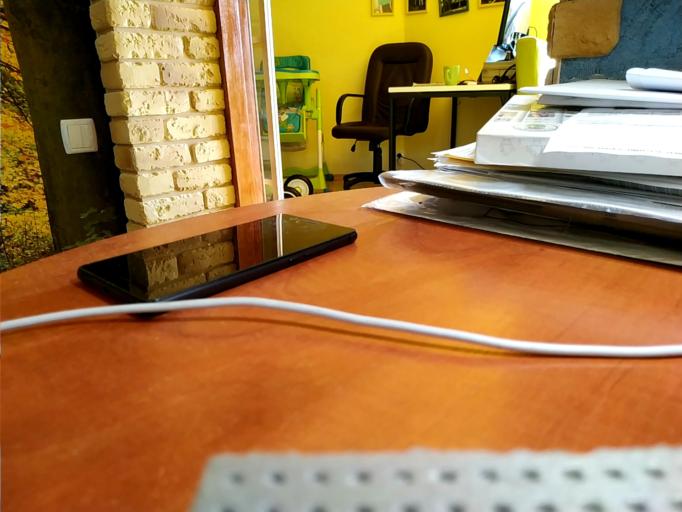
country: RU
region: Tverskaya
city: Kalashnikovo
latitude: 57.3675
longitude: 35.4326
